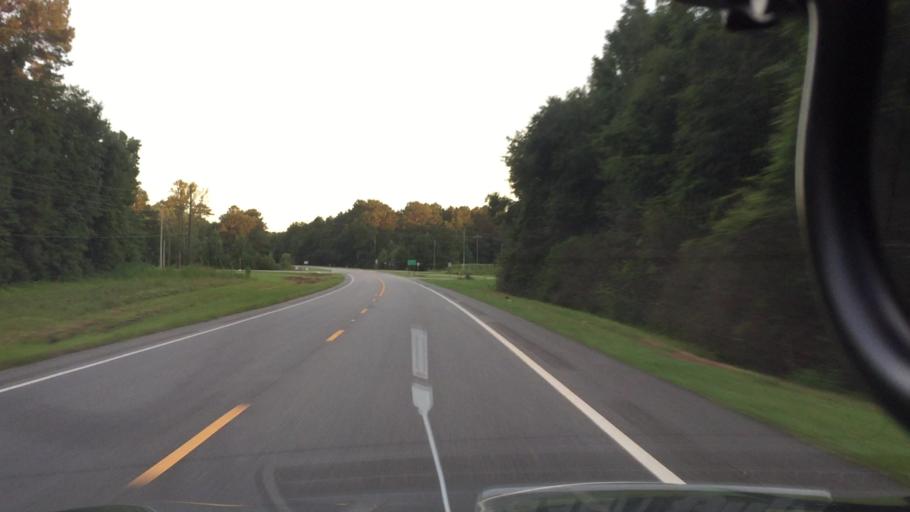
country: US
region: Alabama
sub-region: Coffee County
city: New Brockton
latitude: 31.4913
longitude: -85.9142
